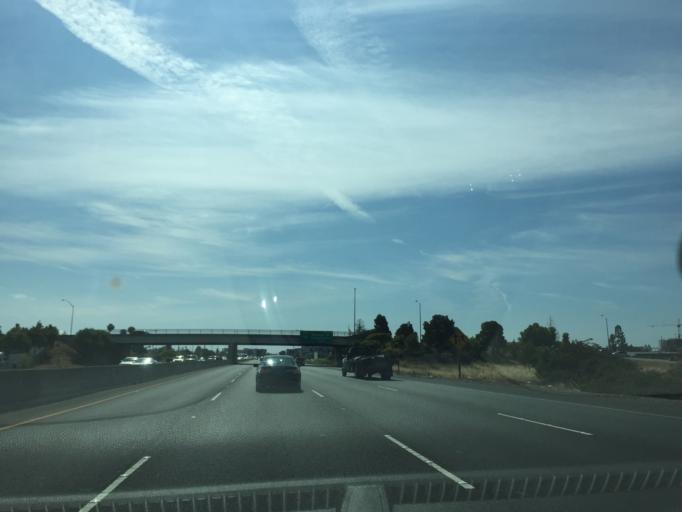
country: US
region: California
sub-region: San Mateo County
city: Redwood City
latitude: 37.4967
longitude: -122.2347
